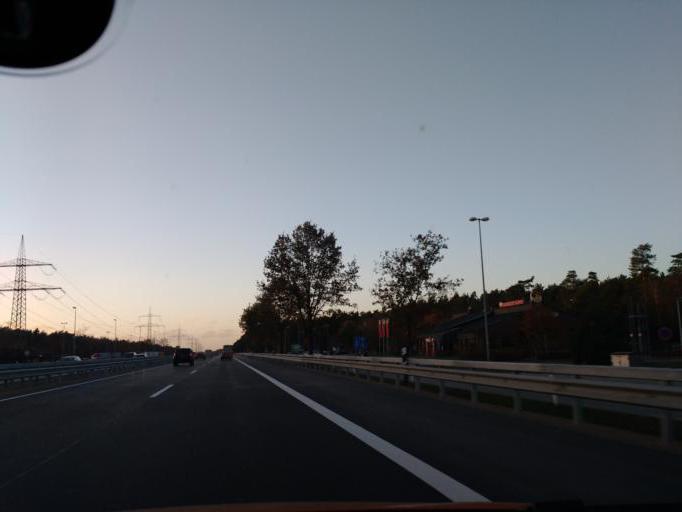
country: DE
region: Schleswig-Holstein
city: Gudow
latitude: 53.5205
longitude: 10.8063
